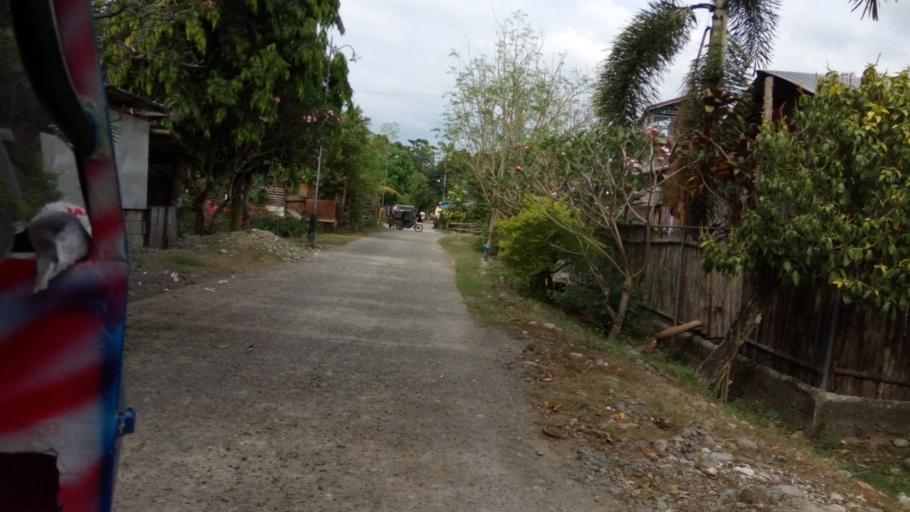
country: PH
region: Ilocos
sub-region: Province of La Union
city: Aringay
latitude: 16.3947
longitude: 120.3520
